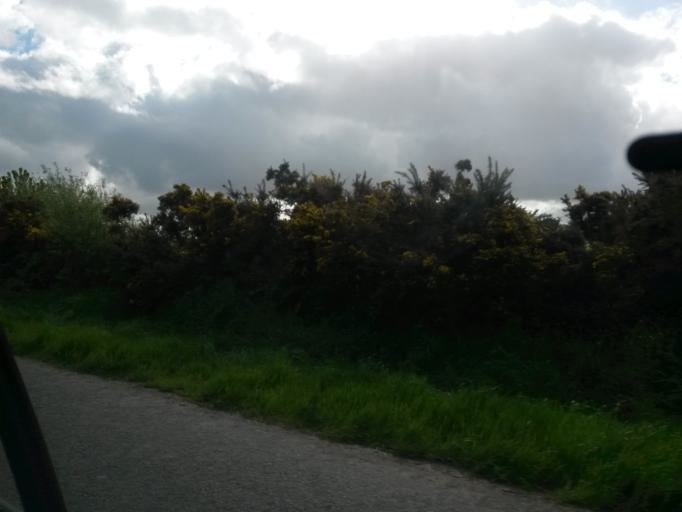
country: IE
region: Leinster
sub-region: Loch Garman
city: Enniscorthy
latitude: 52.5498
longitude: -6.5446
